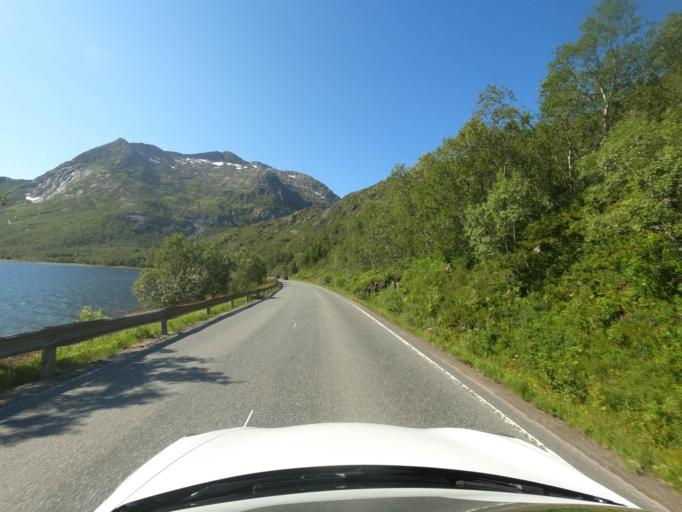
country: NO
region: Nordland
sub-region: Lodingen
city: Lodingen
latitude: 68.5404
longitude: 15.7262
